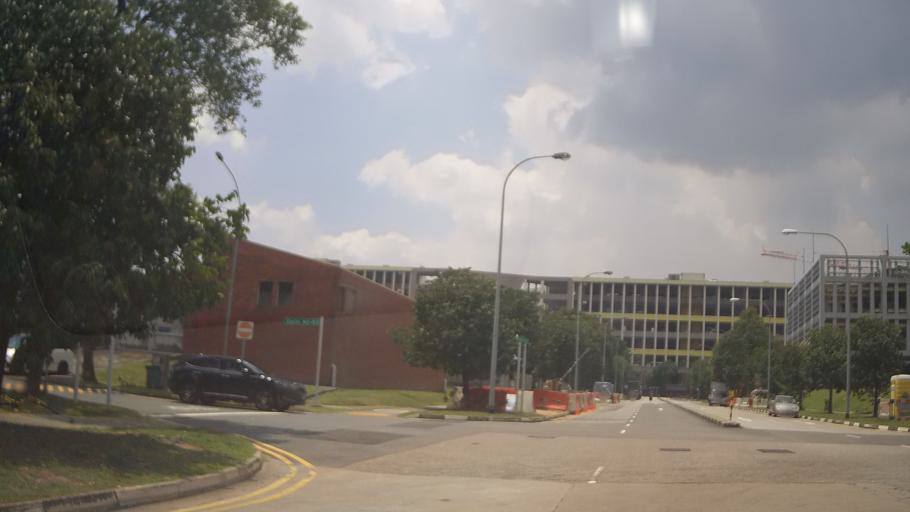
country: MY
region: Johor
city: Johor Bahru
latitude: 1.4525
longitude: 103.8003
